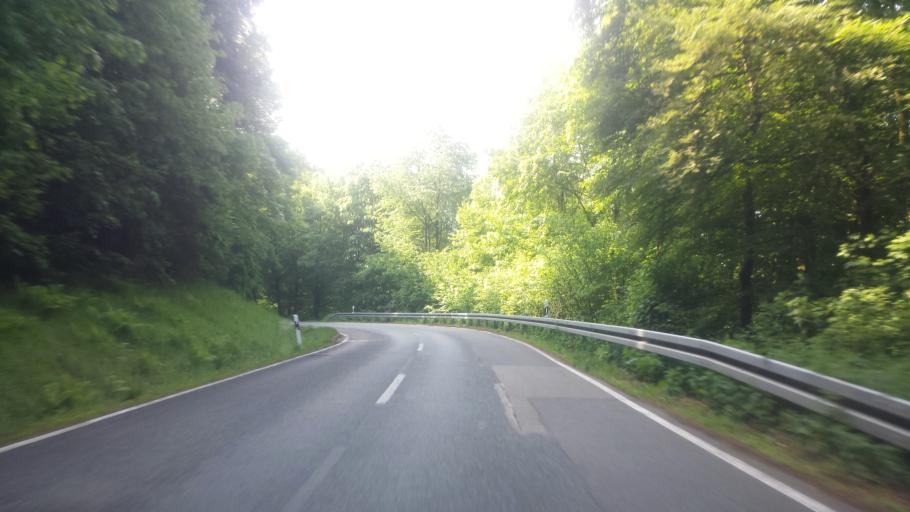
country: DE
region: Hesse
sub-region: Regierungsbezirk Darmstadt
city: Wald-Michelbach
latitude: 49.5725
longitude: 8.8064
